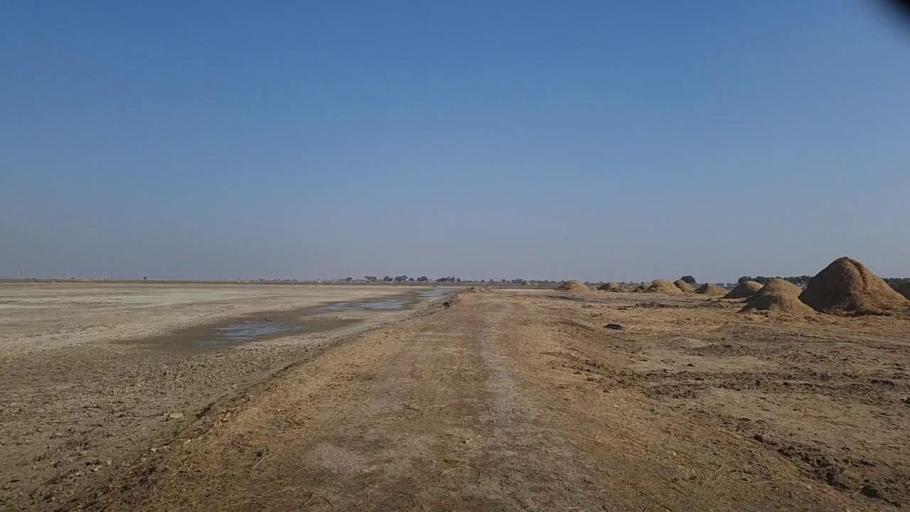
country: PK
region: Sindh
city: Thul
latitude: 28.3589
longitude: 68.7710
